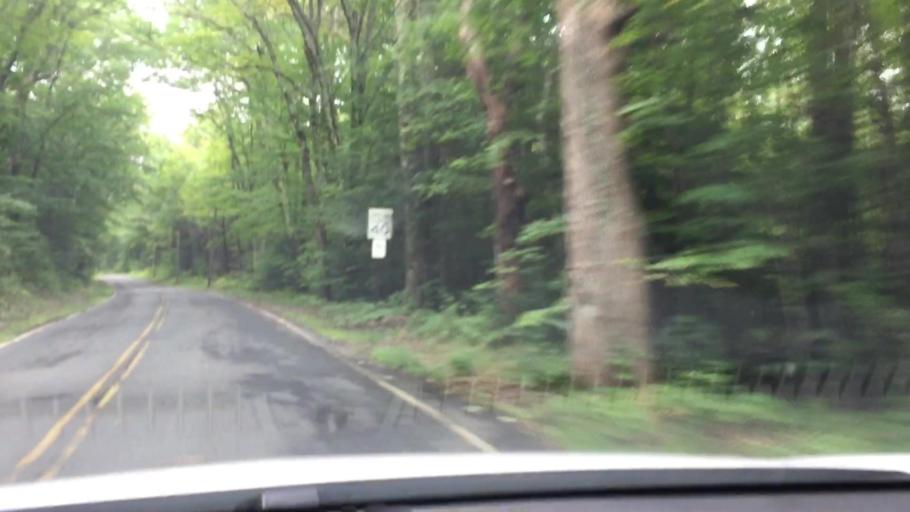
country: US
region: Massachusetts
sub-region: Berkshire County
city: Otis
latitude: 42.2488
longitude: -72.9906
